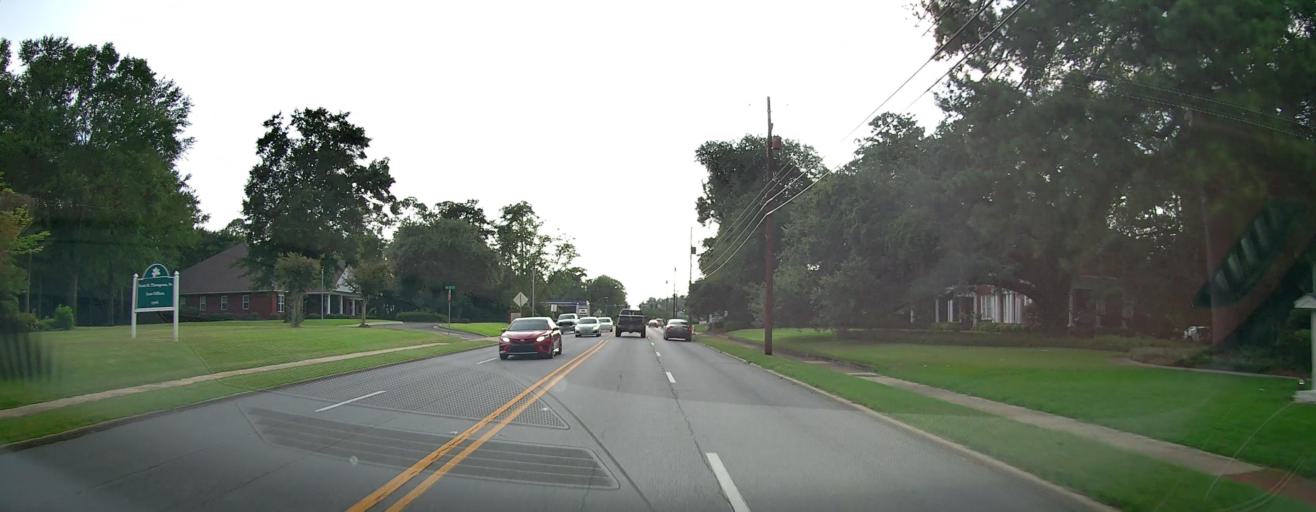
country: US
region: Georgia
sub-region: Laurens County
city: Dublin
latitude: 32.5359
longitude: -82.9236
